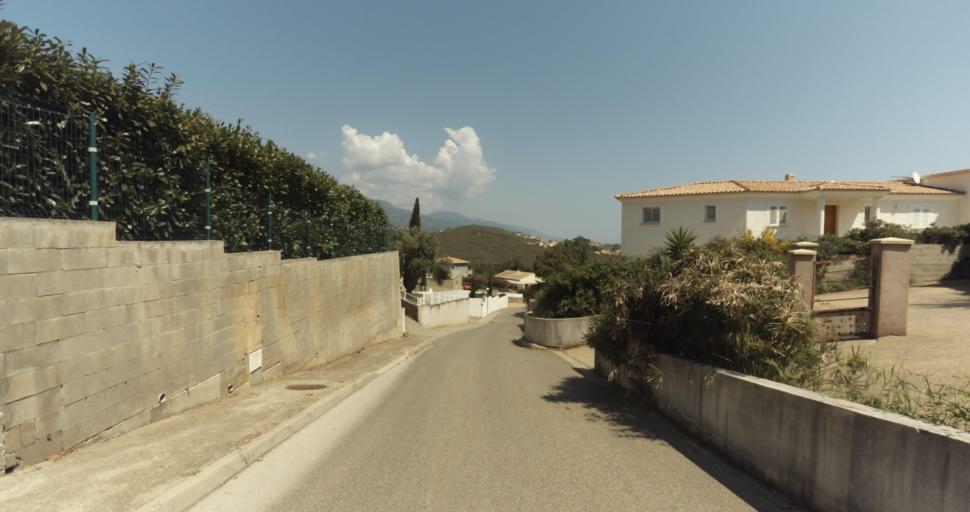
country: FR
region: Corsica
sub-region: Departement de la Haute-Corse
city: Biguglia
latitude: 42.6062
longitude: 9.4279
